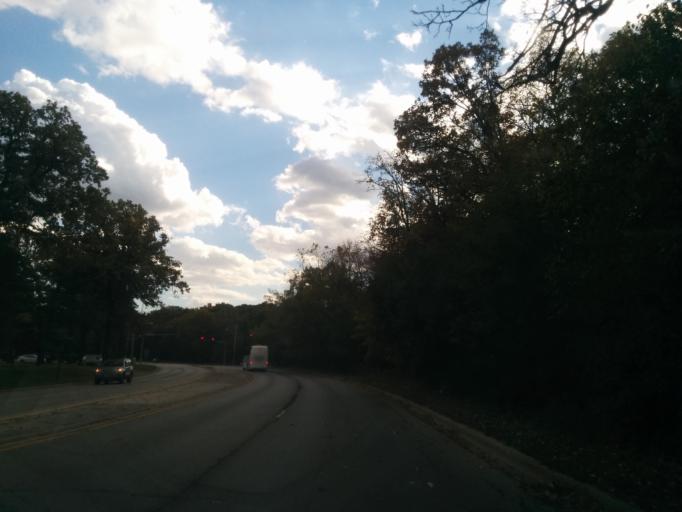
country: US
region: Illinois
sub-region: Cook County
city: Park Ridge
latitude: 41.9975
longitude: -87.8557
